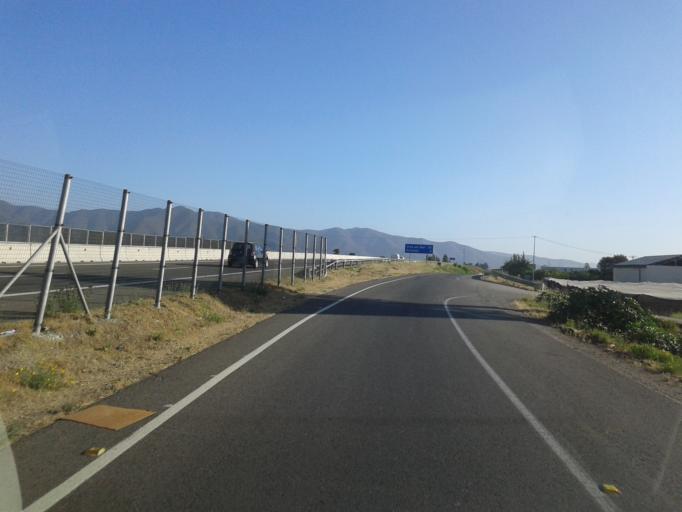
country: CL
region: Valparaiso
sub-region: Provincia de Quillota
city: Quillota
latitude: -32.8567
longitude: -71.2247
